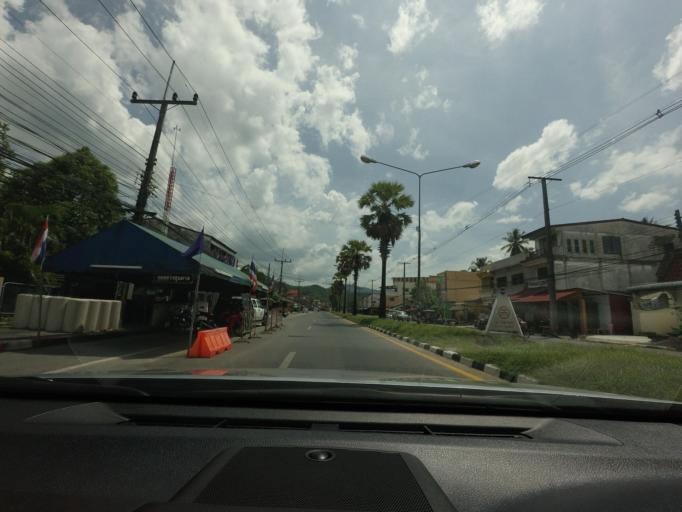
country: TH
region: Yala
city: Raman
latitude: 6.4578
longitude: 101.3445
